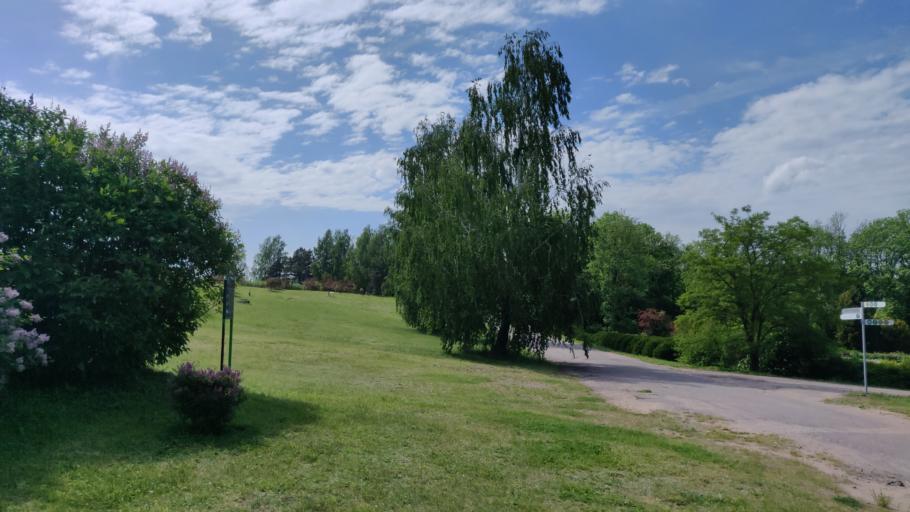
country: LT
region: Vilnius County
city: Rasos
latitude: 54.7314
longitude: 25.4039
